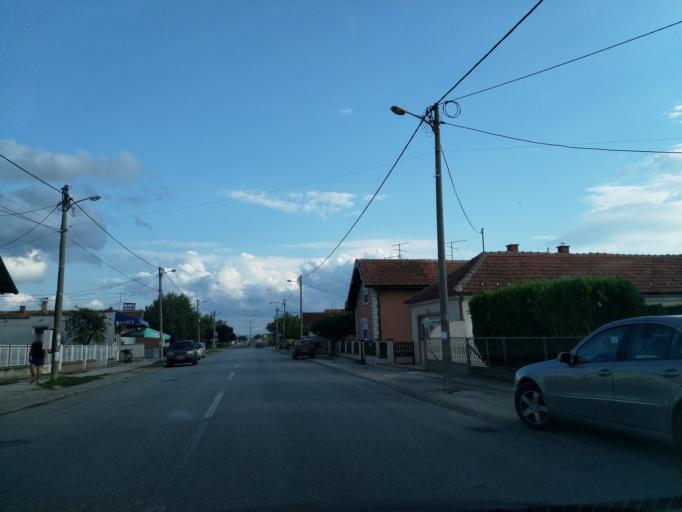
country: RS
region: Central Serbia
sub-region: Pomoravski Okrug
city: Paracin
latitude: 43.8480
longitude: 21.4139
